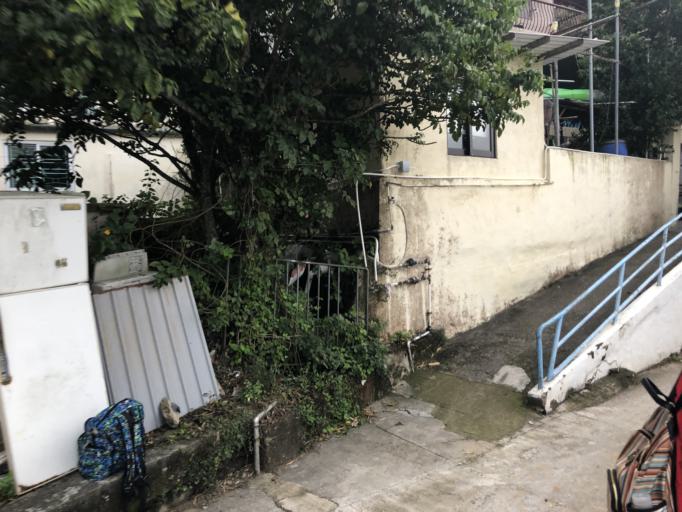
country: HK
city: Tai O
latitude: 22.2470
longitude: 113.8620
